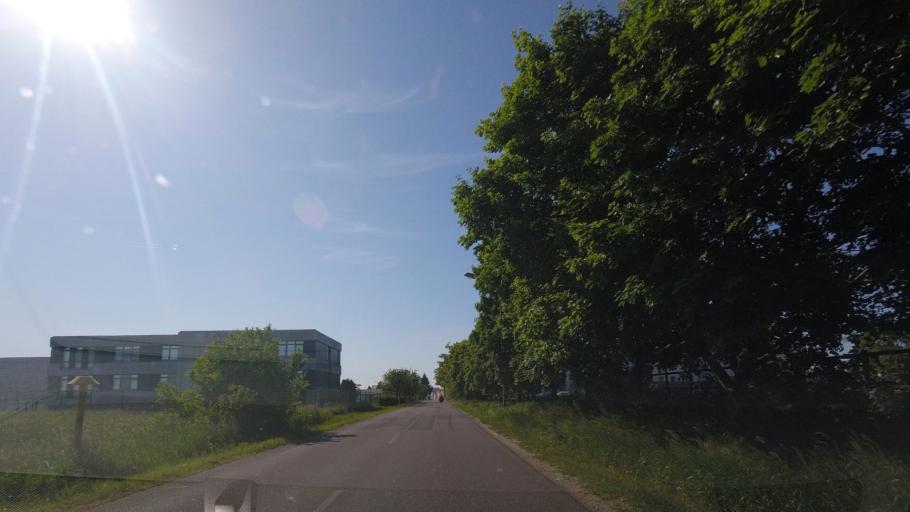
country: DE
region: Brandenburg
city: Brandenburg an der Havel
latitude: 52.3870
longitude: 12.5997
